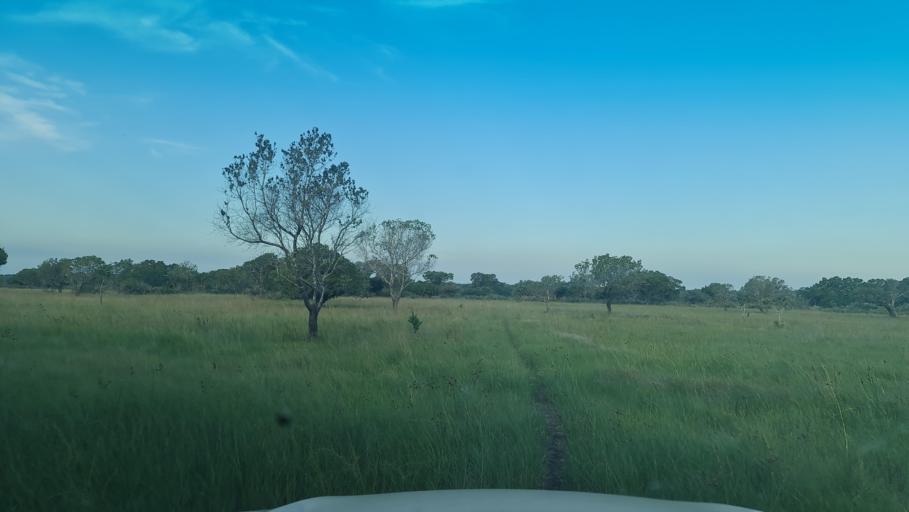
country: MZ
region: Gaza
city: Macia
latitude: -25.2143
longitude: 33.0533
